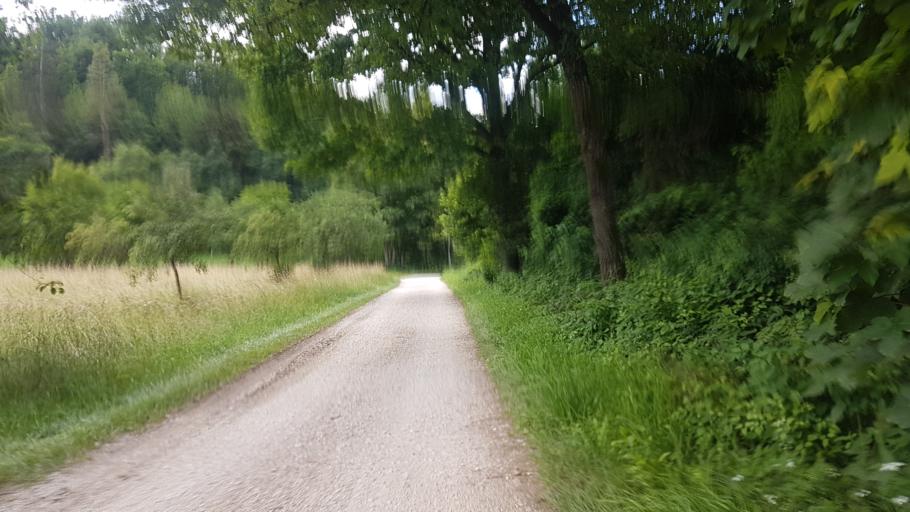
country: DE
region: Bavaria
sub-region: Regierungsbezirk Mittelfranken
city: Pappenheim
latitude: 48.9205
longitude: 10.9834
